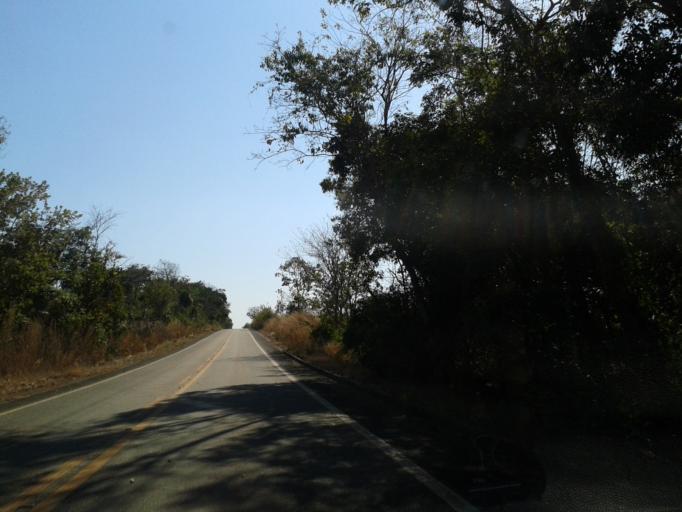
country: BR
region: Goias
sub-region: Mozarlandia
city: Mozarlandia
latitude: -14.6844
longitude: -50.5401
